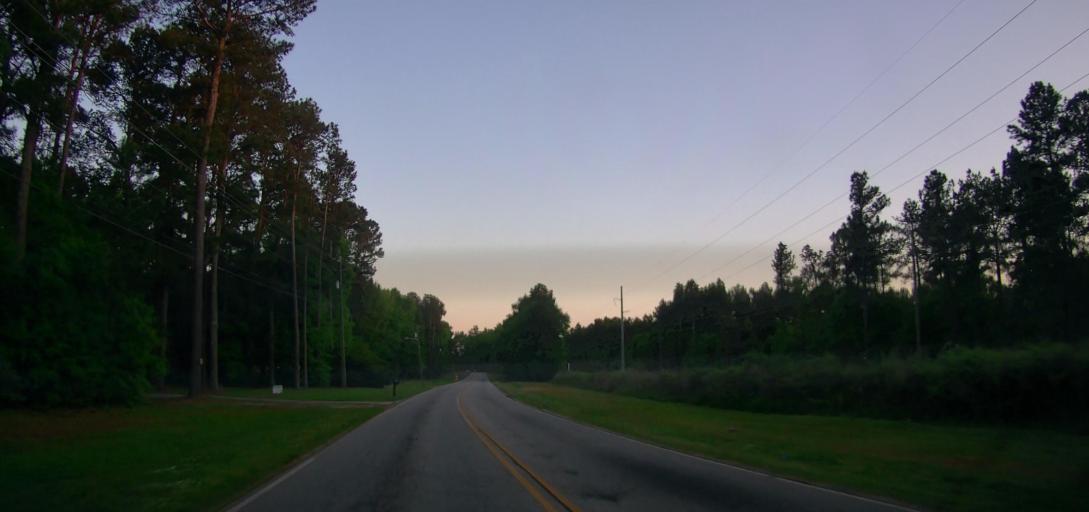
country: US
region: Georgia
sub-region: Henry County
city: McDonough
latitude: 33.4421
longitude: -84.1877
